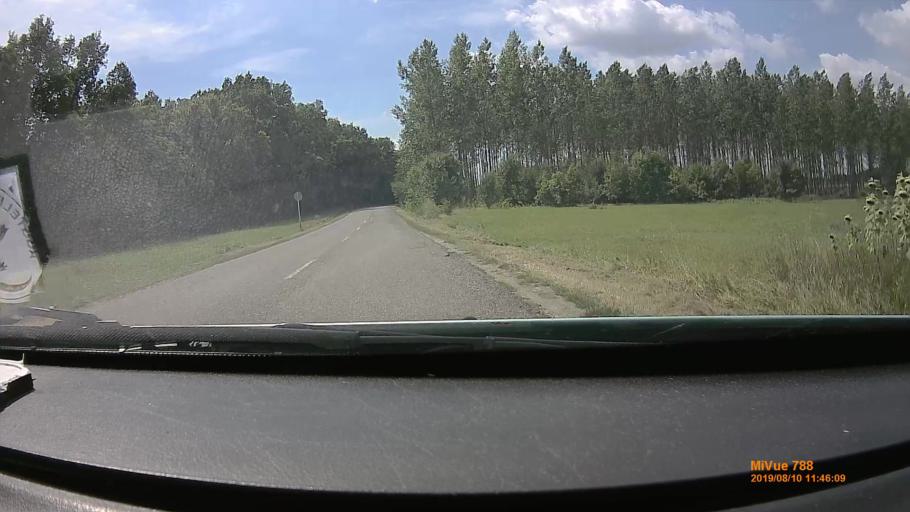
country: HU
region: Borsod-Abauj-Zemplen
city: Szentistvan
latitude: 47.7134
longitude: 20.6330
